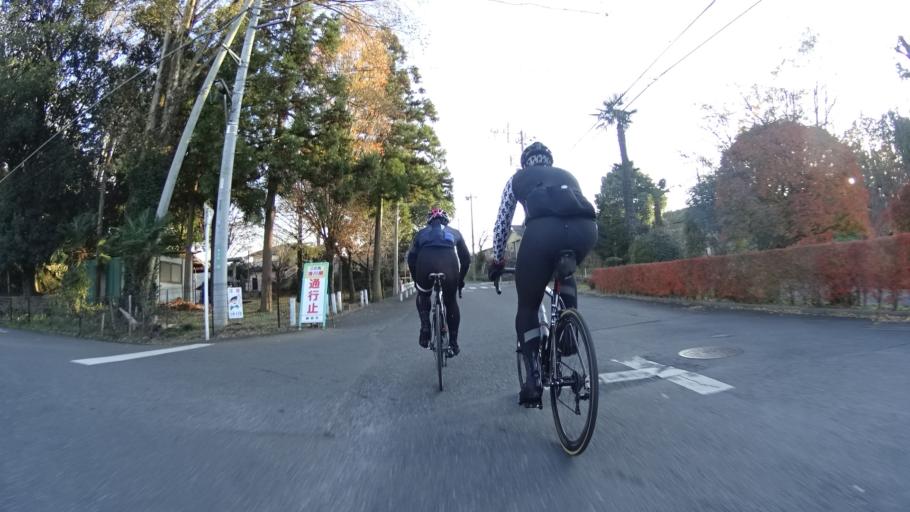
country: JP
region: Saitama
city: Hanno
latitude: 35.8401
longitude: 139.3186
